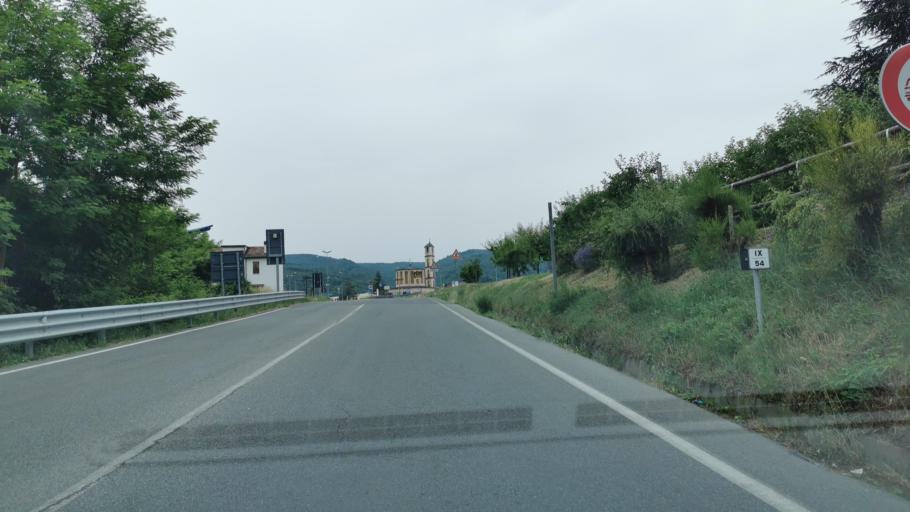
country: IT
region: Piedmont
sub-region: Provincia di Cuneo
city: Ceva
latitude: 44.3792
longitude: 8.0416
